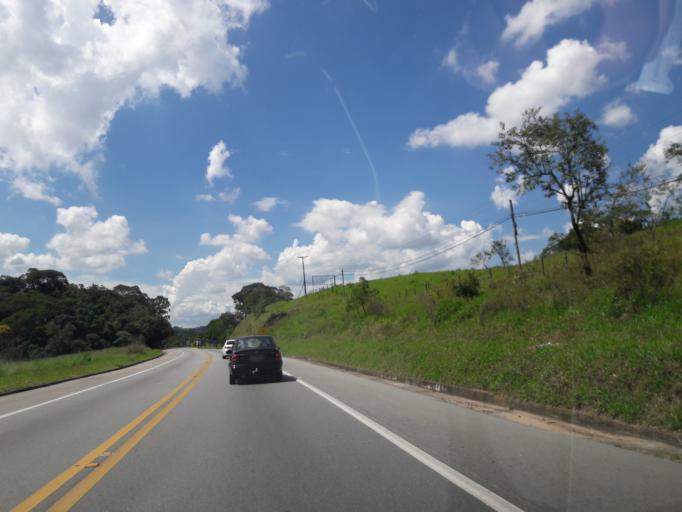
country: BR
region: Sao Paulo
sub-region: Francisco Morato
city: Francisco Morato
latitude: -23.3088
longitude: -46.8138
